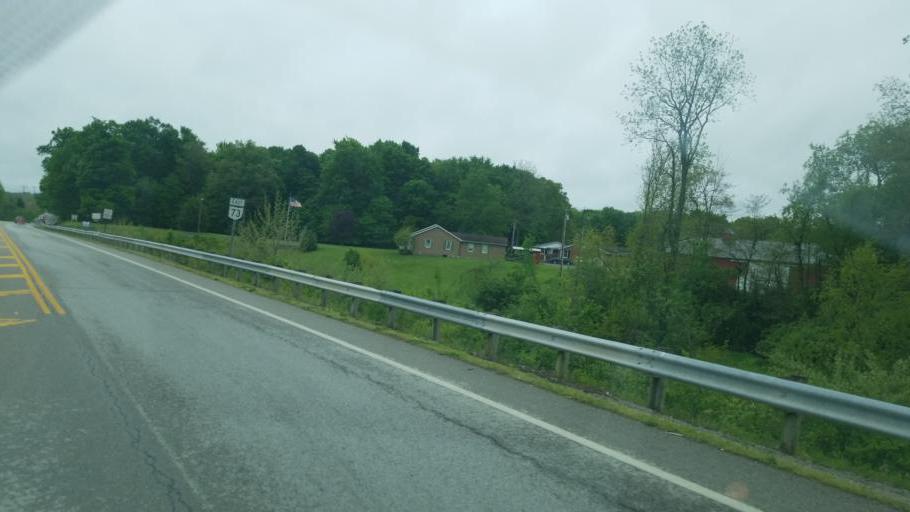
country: US
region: Ohio
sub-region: Highland County
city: Hillsboro
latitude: 39.2246
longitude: -83.6246
